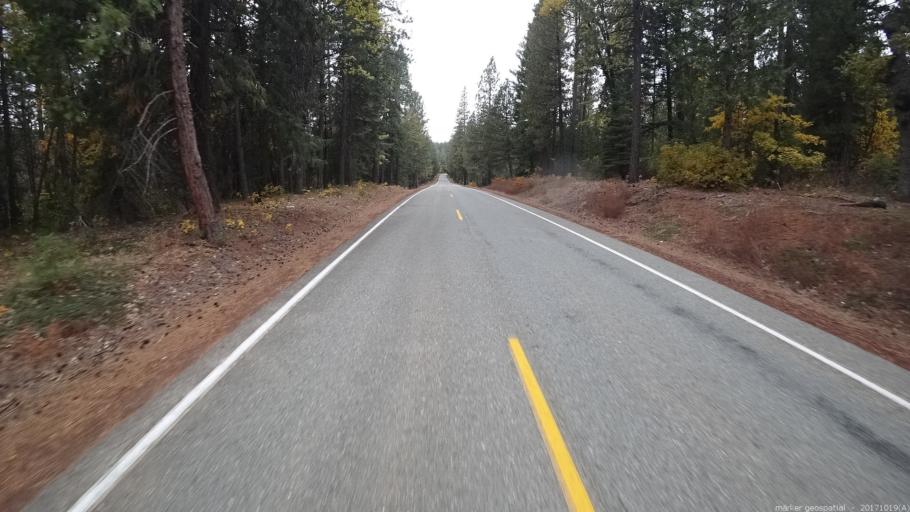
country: US
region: California
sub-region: Shasta County
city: Burney
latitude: 41.1180
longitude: -121.5826
